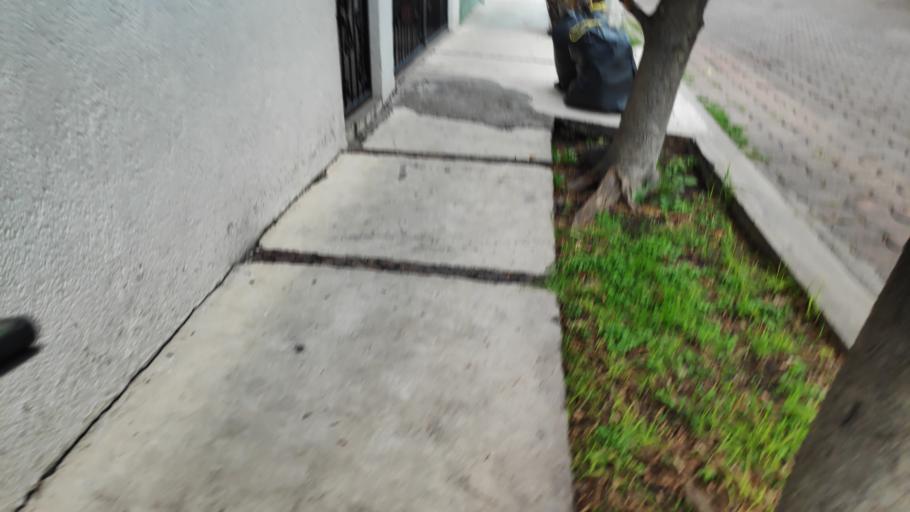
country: MX
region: Queretaro
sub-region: Queretaro
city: Santiago de Queretaro
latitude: 20.5866
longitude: -100.3687
